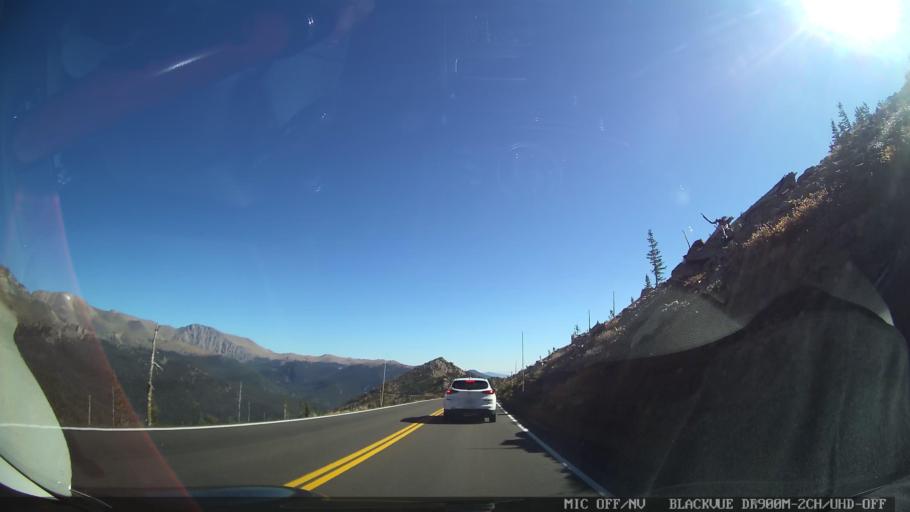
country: US
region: Colorado
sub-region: Larimer County
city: Estes Park
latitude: 40.3967
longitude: -105.6792
